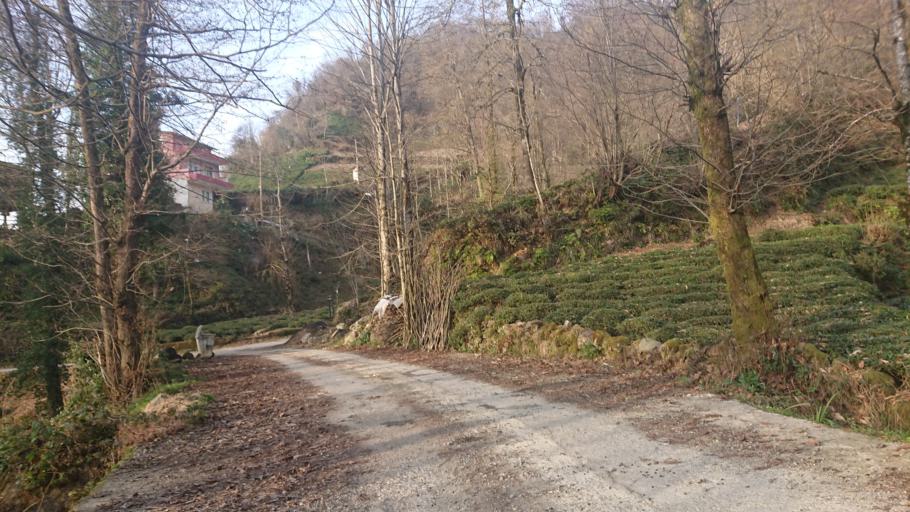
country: TR
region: Rize
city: Rize
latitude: 40.9806
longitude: 40.4968
